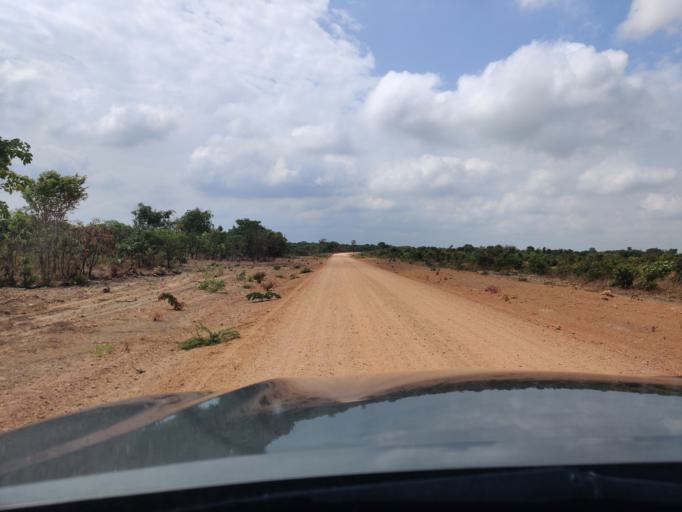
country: ZM
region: Central
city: Mkushi
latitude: -13.6578
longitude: 29.7519
